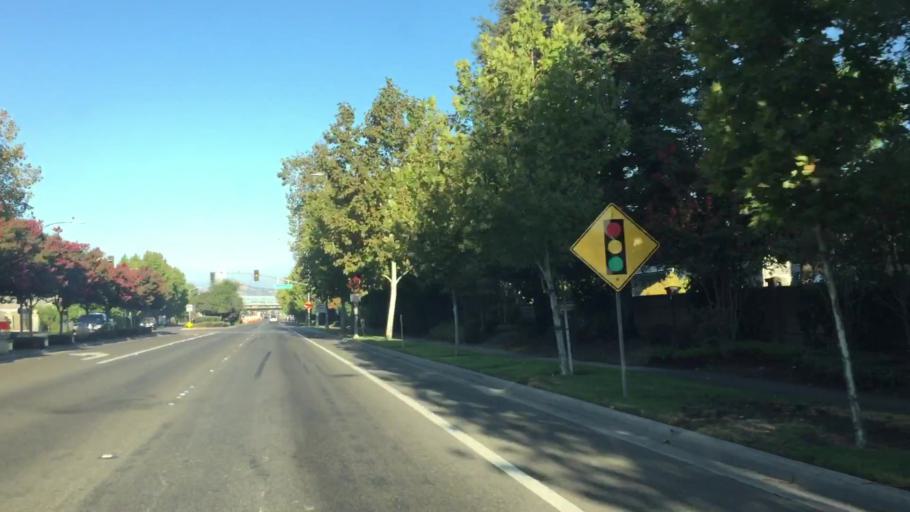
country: US
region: California
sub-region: Contra Costa County
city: Brentwood
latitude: 37.9254
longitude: -121.7274
